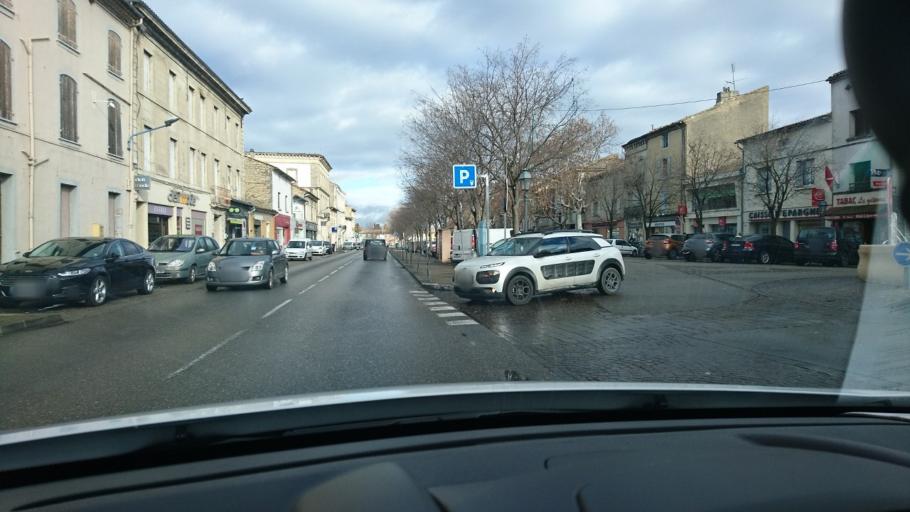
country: FR
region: Languedoc-Roussillon
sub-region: Departement du Gard
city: Pont-Saint-Esprit
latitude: 44.2565
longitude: 4.6476
